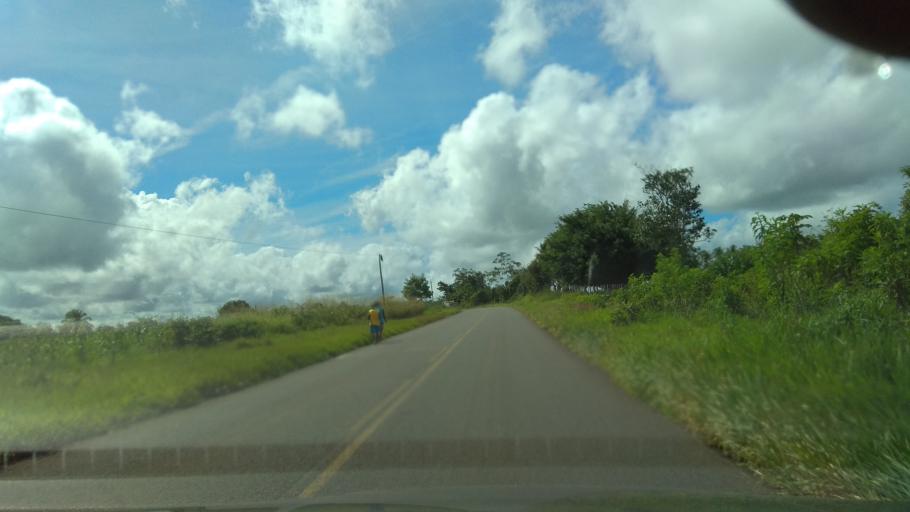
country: BR
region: Bahia
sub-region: Mutuipe
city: Mutuipe
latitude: -13.1666
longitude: -39.3347
